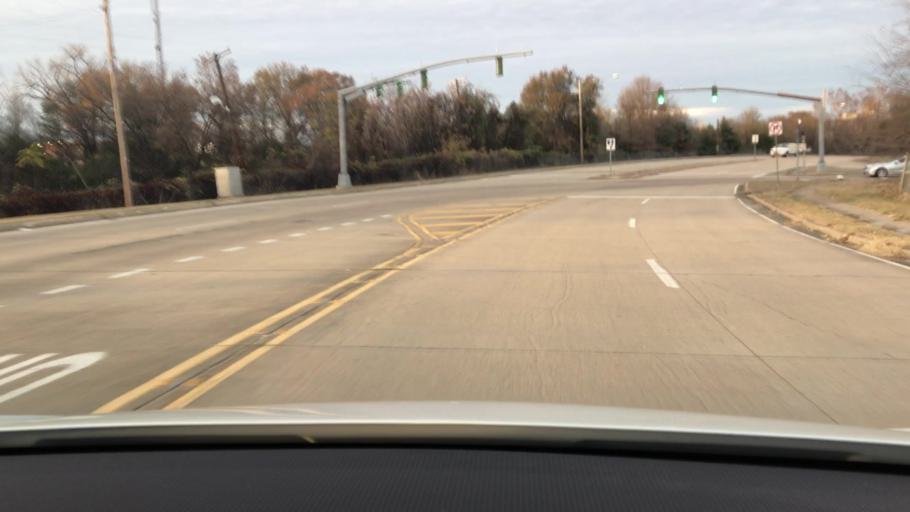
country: US
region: Louisiana
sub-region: Caddo Parish
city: Shreveport
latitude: 32.5003
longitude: -93.7528
